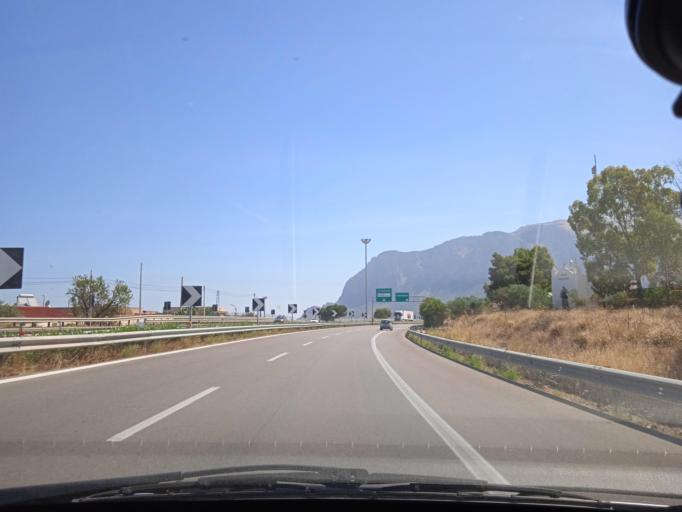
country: IT
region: Sicily
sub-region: Palermo
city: Agliandroni-Paternella
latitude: 38.1350
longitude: 13.0767
